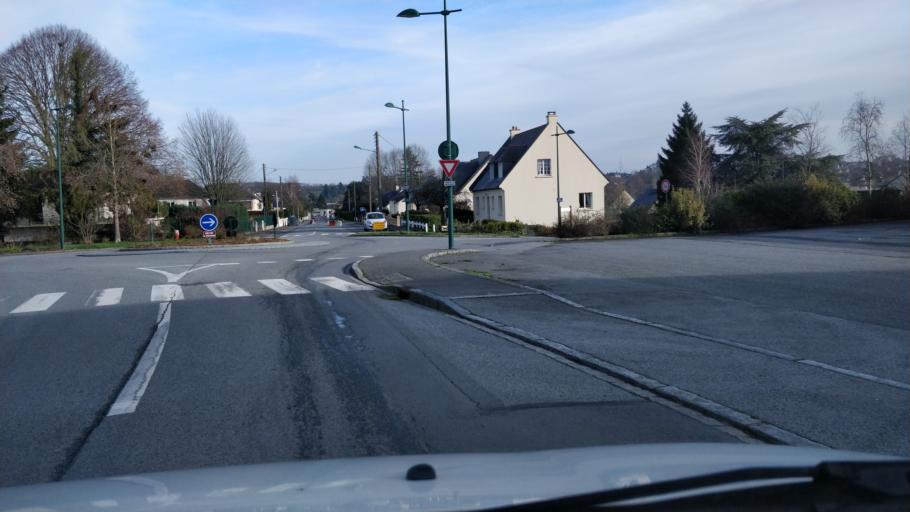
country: FR
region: Brittany
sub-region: Departement d'Ille-et-Vilaine
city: Argentre-du-Plessis
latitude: 48.0536
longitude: -1.1594
